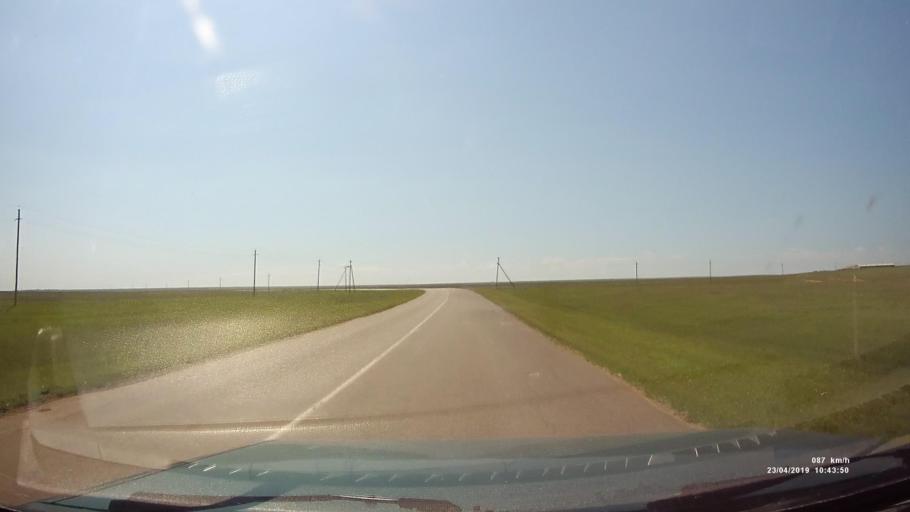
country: RU
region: Kalmykiya
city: Yashalta
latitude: 46.4652
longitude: 42.6502
